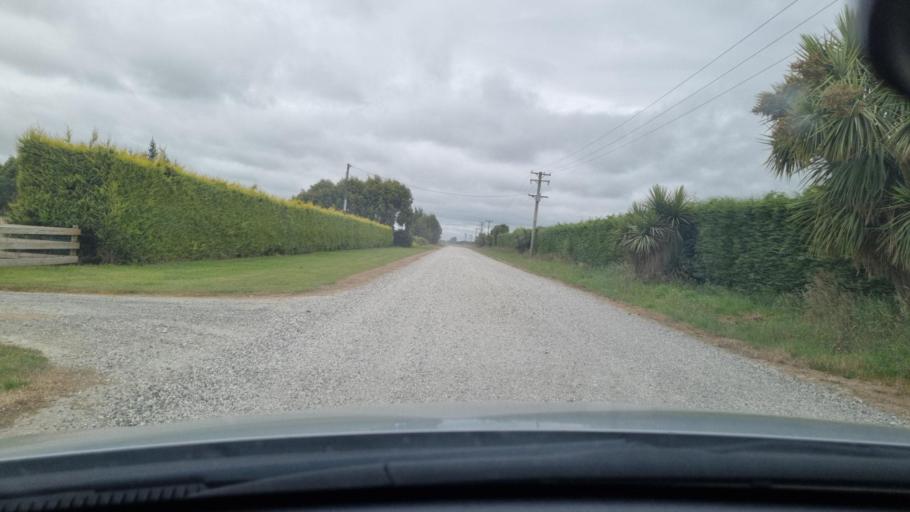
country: NZ
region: Southland
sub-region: Invercargill City
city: Invercargill
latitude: -46.3740
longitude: 168.2985
